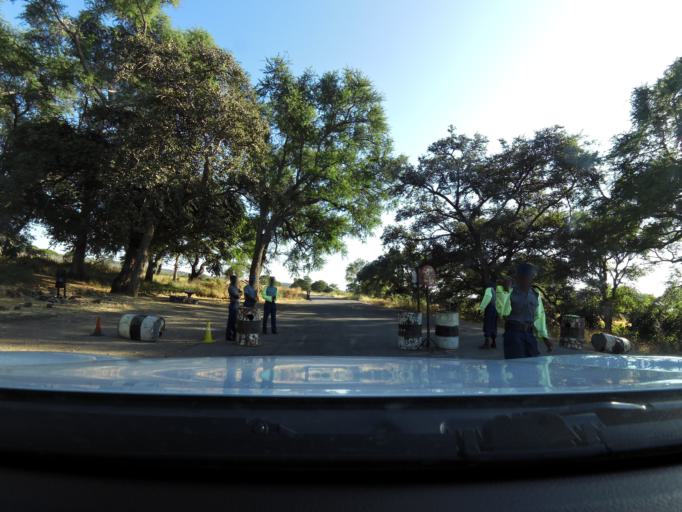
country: ZW
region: Matabeleland North
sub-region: Hwange District
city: Victoria Falls
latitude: -18.2128
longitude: 26.0306
